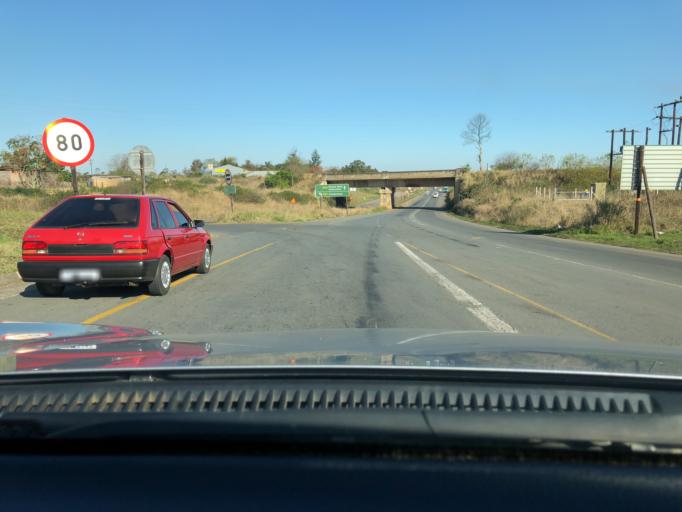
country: ZA
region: KwaZulu-Natal
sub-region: uMgungundlovu District Municipality
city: Camperdown
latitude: -29.7210
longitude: 30.4979
